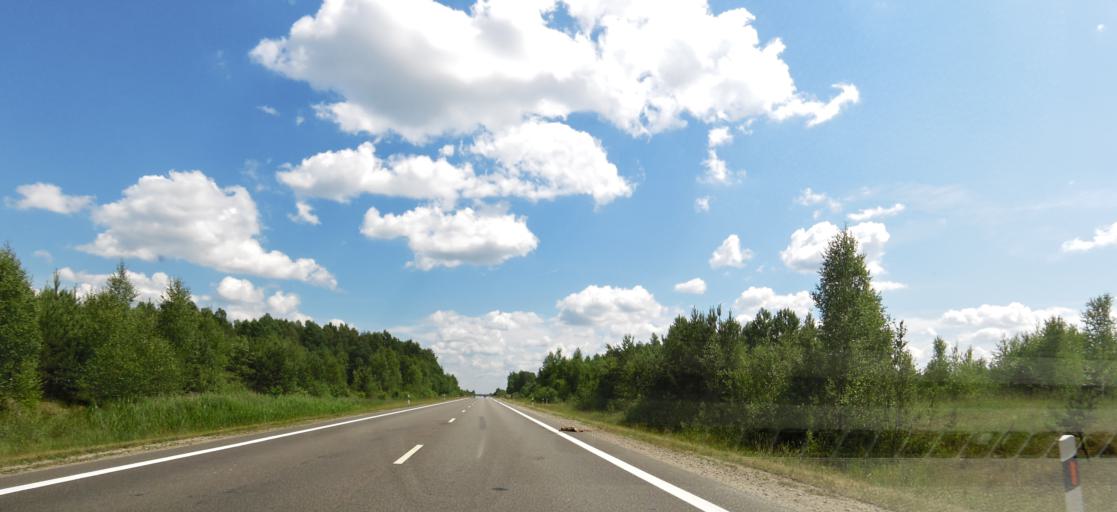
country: LT
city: Skaidiskes
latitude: 54.5718
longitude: 25.6194
